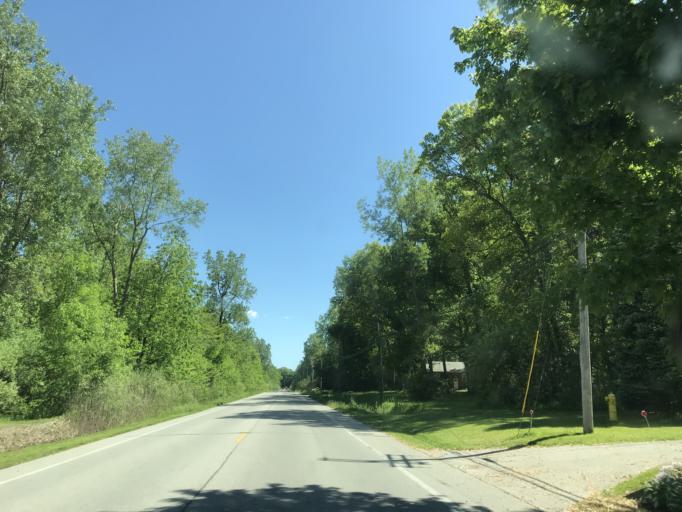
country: US
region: Michigan
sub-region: Wayne County
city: Woodhaven
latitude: 42.1734
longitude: -83.2865
